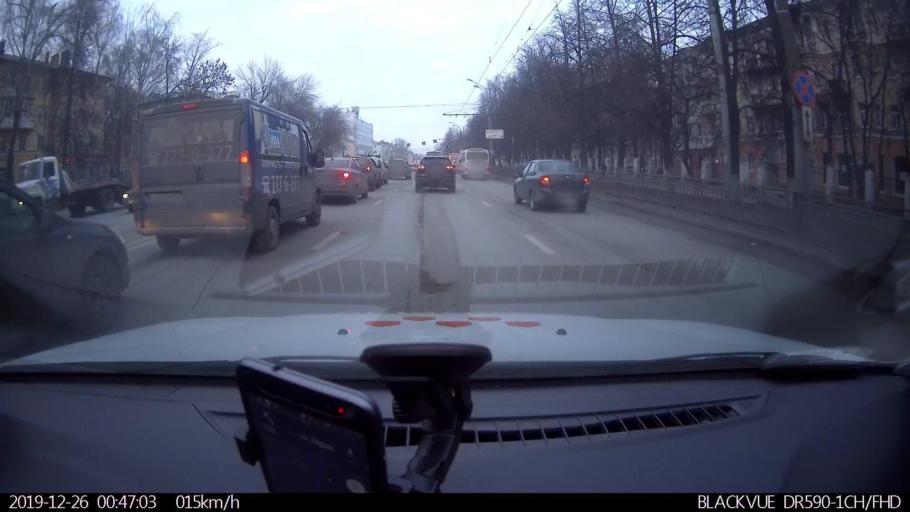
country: RU
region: Nizjnij Novgorod
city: Nizhniy Novgorod
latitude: 56.3022
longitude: 43.9845
